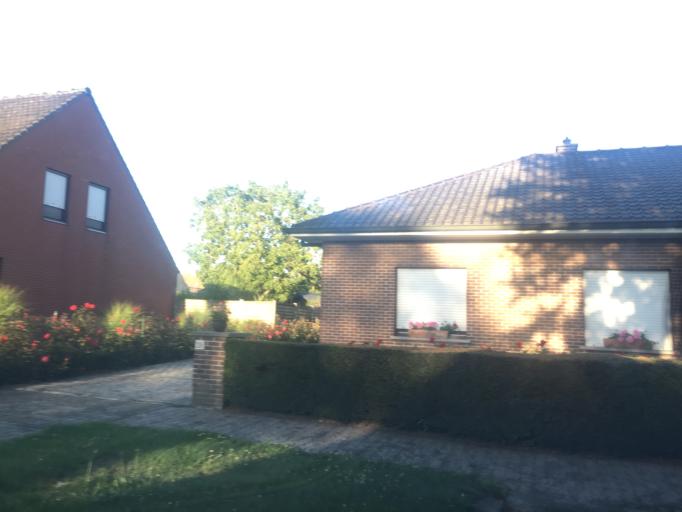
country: BE
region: Flanders
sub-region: Provincie West-Vlaanderen
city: Izegem
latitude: 50.9159
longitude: 3.2023
